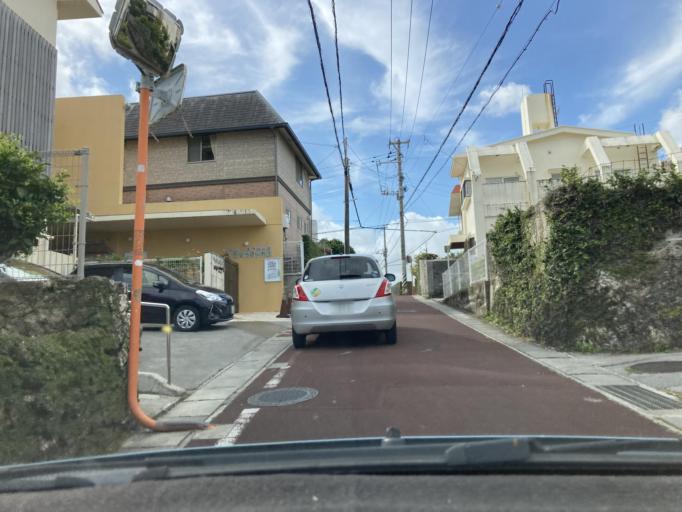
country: JP
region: Okinawa
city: Naha-shi
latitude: 26.2217
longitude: 127.7181
